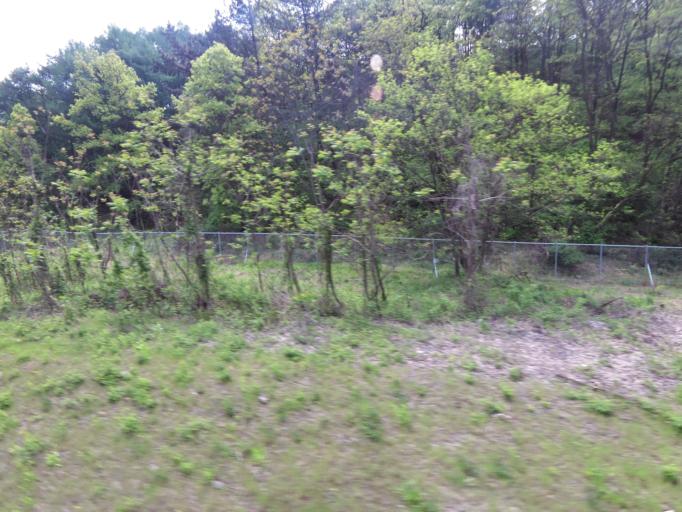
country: KR
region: Daejeon
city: Daejeon
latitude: 36.3389
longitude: 127.4958
